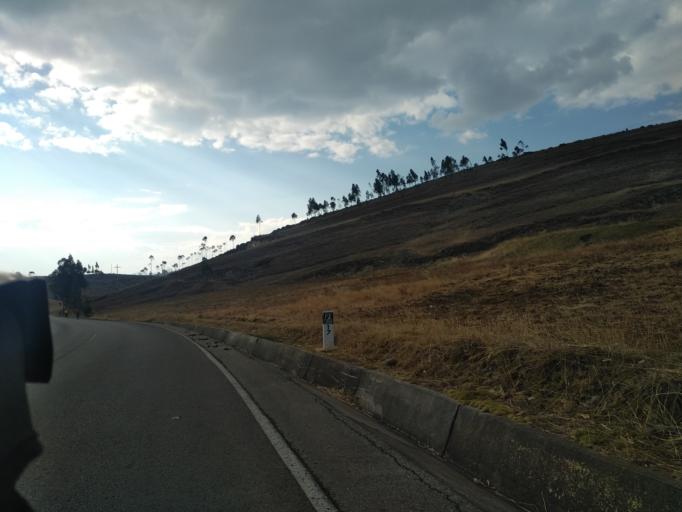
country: PE
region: Cajamarca
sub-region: Provincia de Cajamarca
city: Llacanora
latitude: -7.1452
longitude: -78.3997
